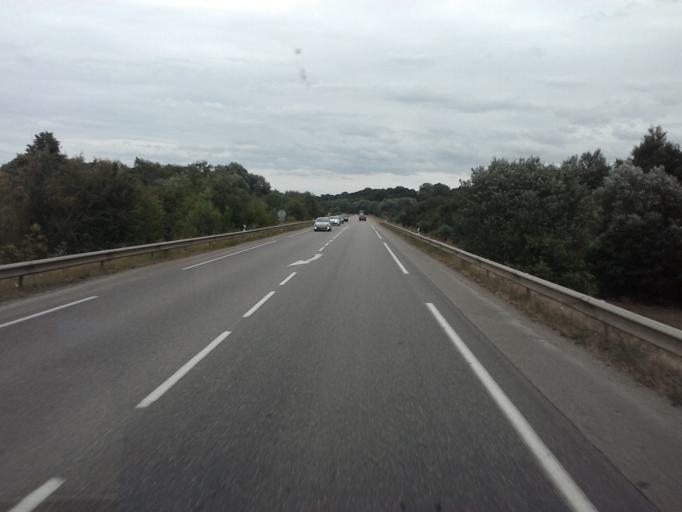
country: FR
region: Lorraine
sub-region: Departement de Meurthe-et-Moselle
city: Messein
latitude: 48.6011
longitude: 6.1250
